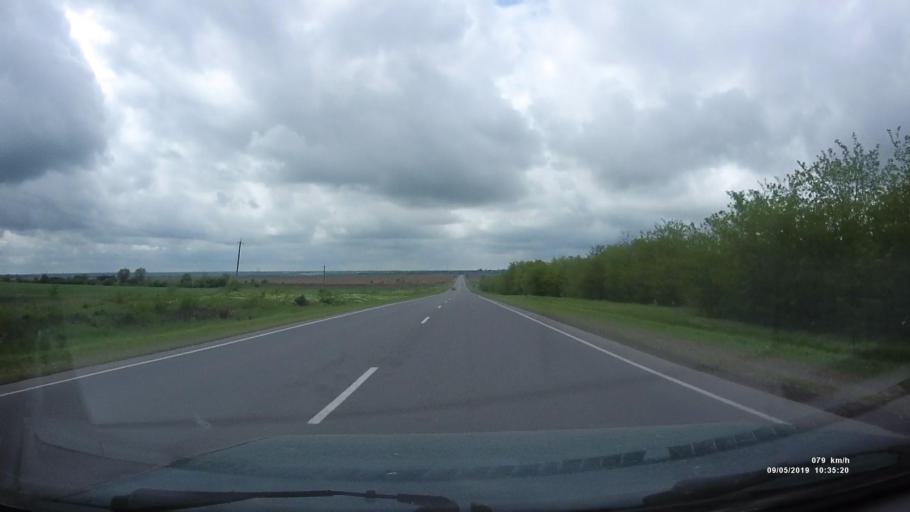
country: RU
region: Rostov
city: Peshkovo
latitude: 47.0440
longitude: 39.4140
